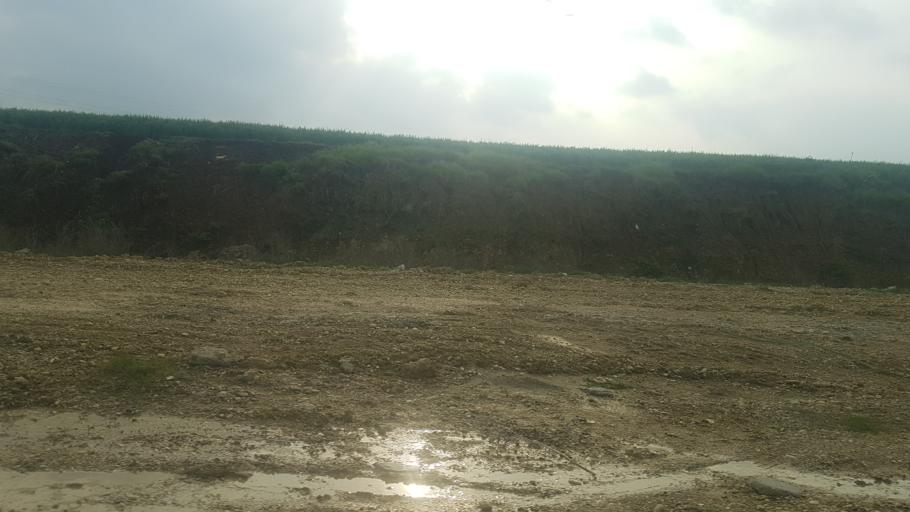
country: TR
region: Adana
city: Seyhan
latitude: 37.0479
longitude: 35.2104
